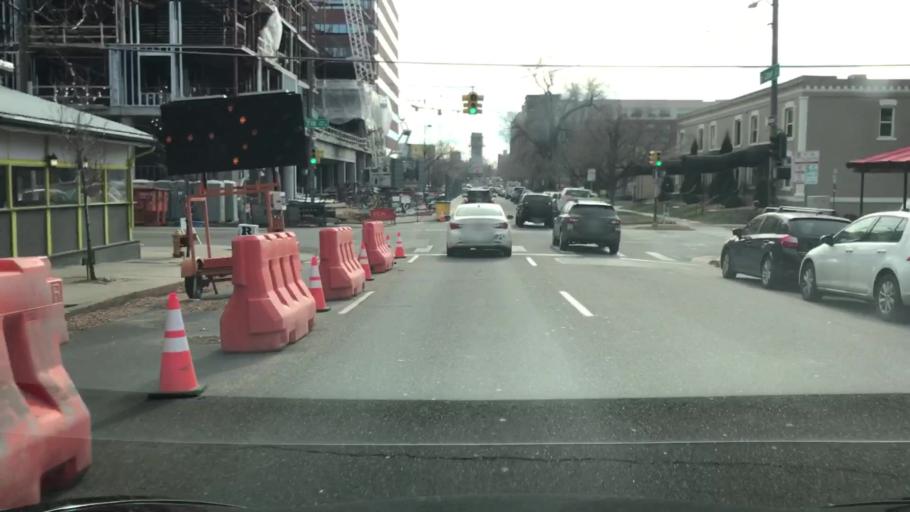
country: US
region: Colorado
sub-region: Denver County
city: Denver
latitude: 39.7276
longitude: -104.9837
